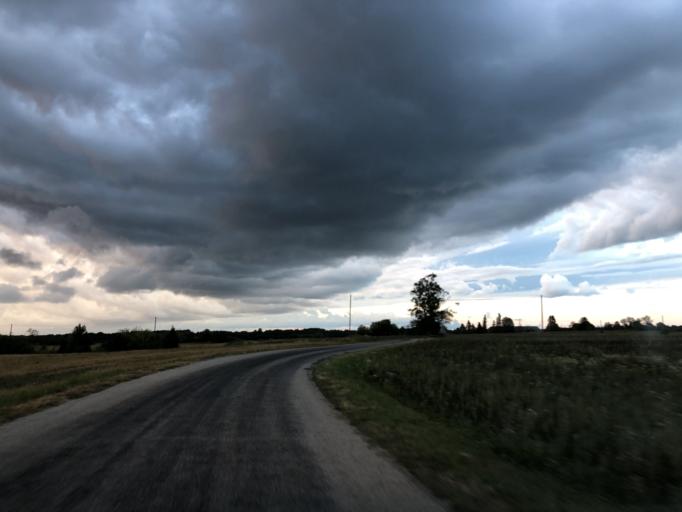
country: EE
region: Laeaene
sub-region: Ridala Parish
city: Uuemoisa
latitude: 58.8829
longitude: 23.6491
